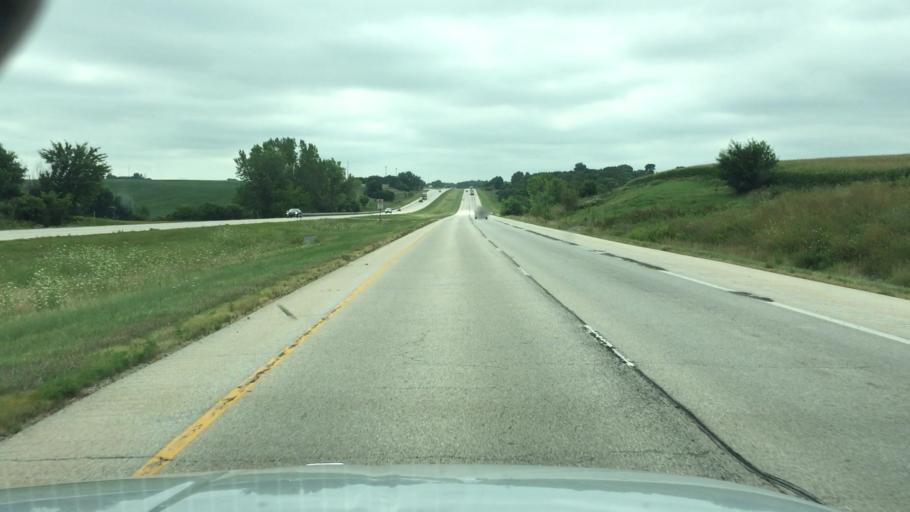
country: US
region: Illinois
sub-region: Henry County
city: Orion
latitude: 41.2254
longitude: -90.3319
